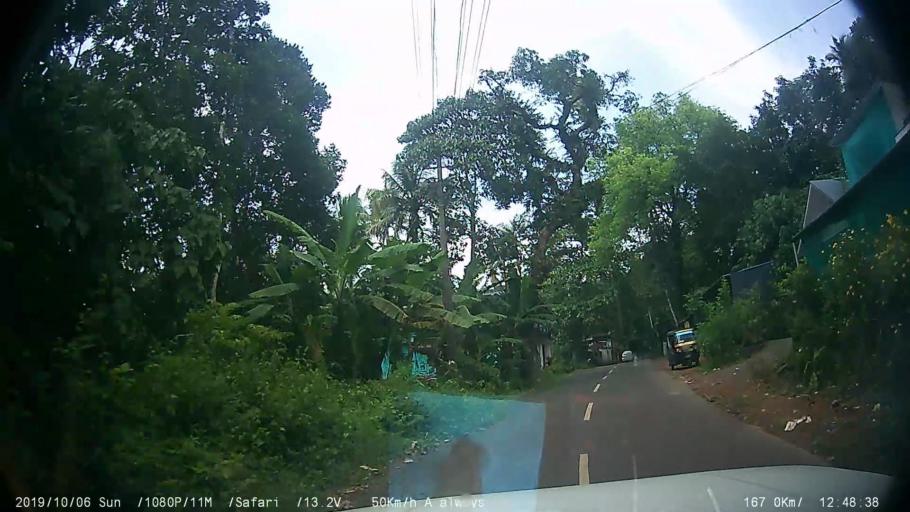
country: IN
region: Kerala
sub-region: Kottayam
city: Palackattumala
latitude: 9.7807
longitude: 76.5973
